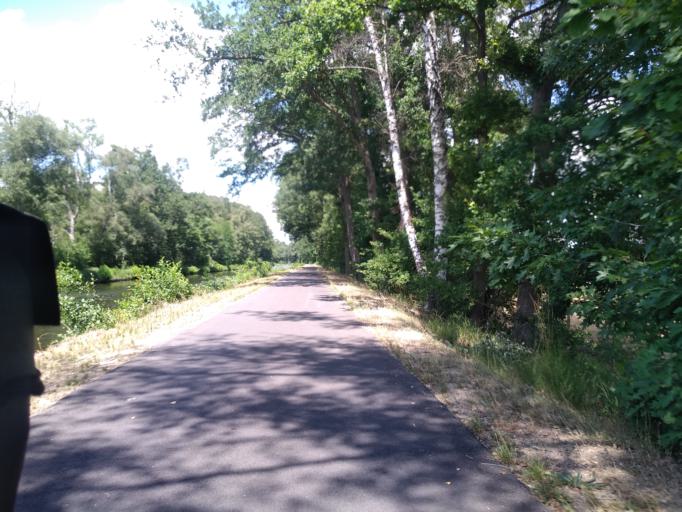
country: FR
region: Rhone-Alpes
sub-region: Departement de la Loire
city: Mably
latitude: 46.1144
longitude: 4.0789
